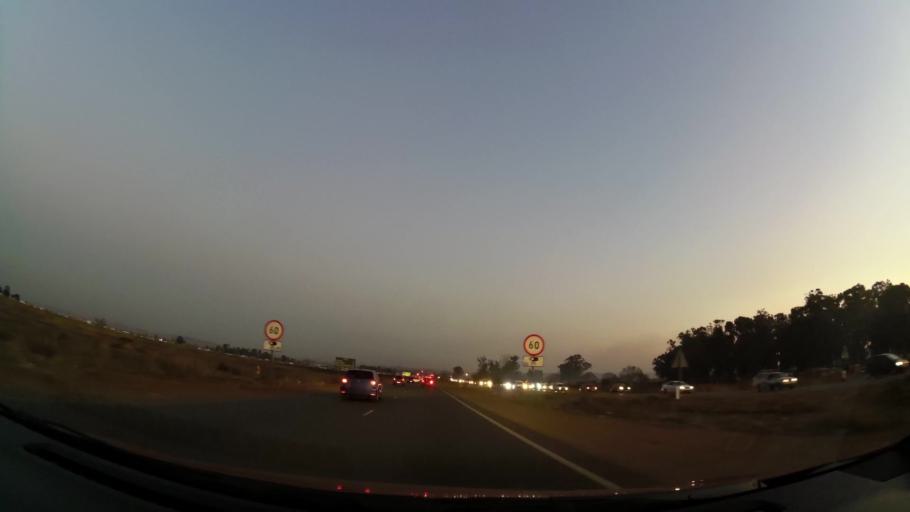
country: ZA
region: Gauteng
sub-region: City of Johannesburg Metropolitan Municipality
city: Soweto
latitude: -26.2942
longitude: 27.8157
